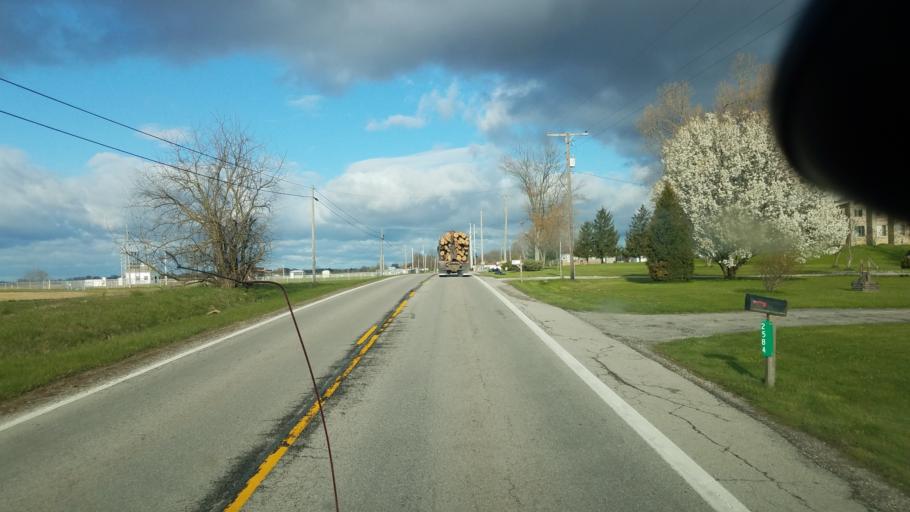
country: US
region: Ohio
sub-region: Marion County
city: Marion
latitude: 40.6126
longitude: -83.1992
